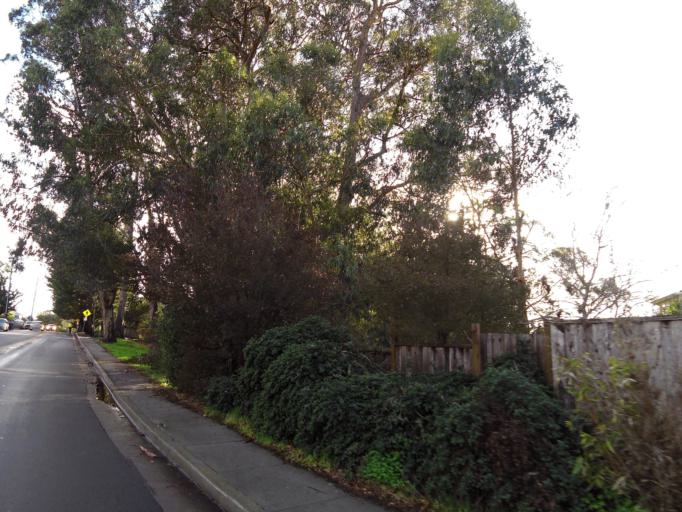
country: US
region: California
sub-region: Santa Cruz County
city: Santa Cruz
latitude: 36.9659
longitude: -122.0566
